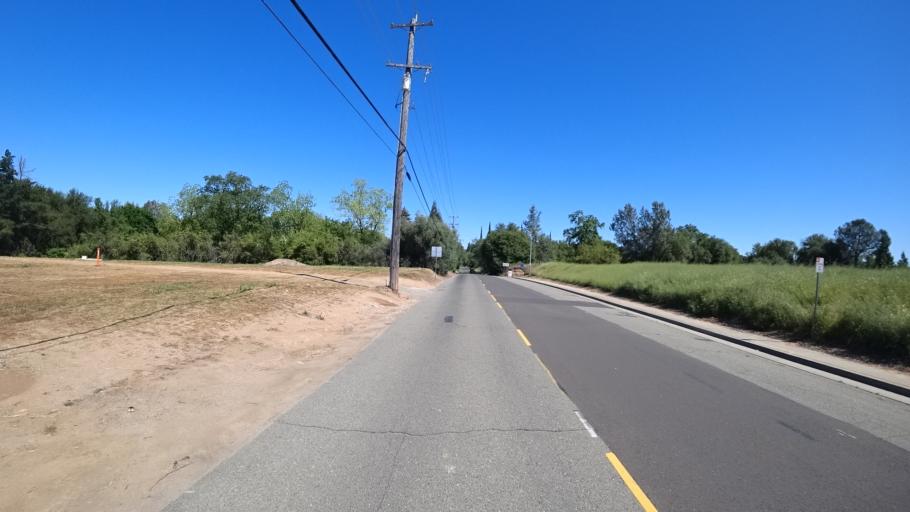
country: US
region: California
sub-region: Placer County
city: Rocklin
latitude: 38.8098
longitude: -121.2194
